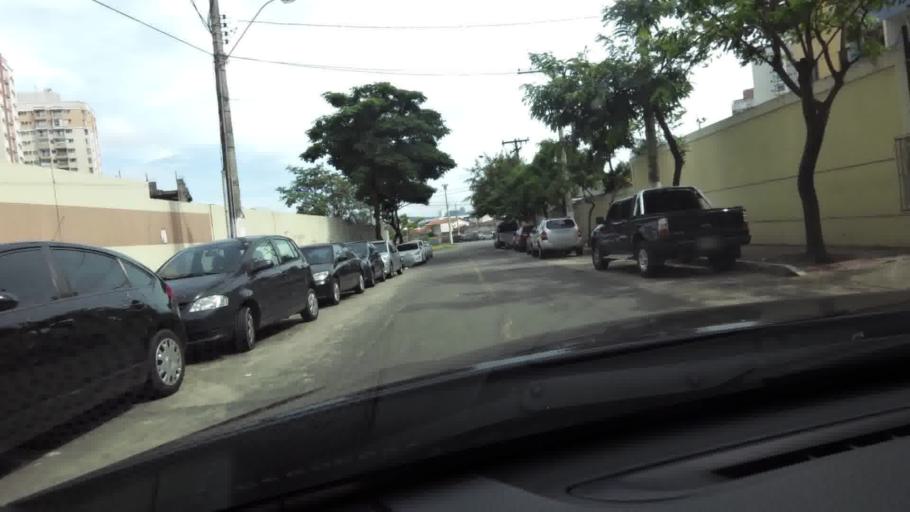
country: BR
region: Espirito Santo
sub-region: Vila Velha
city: Vila Velha
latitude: -20.3561
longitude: -40.2912
